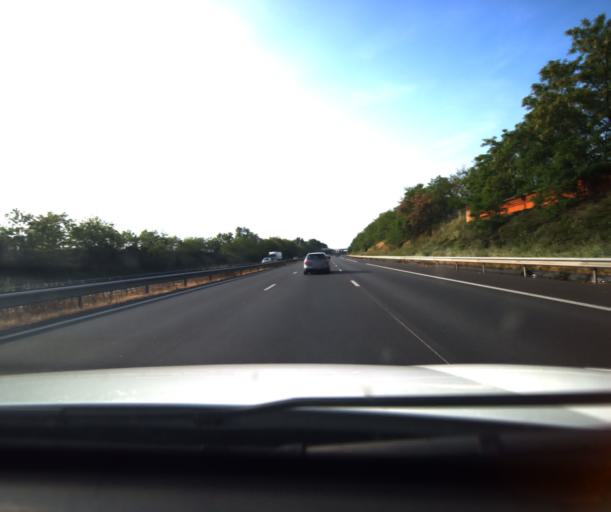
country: FR
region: Midi-Pyrenees
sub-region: Departement de la Haute-Garonne
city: Aucamville
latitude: 43.6743
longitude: 1.4166
